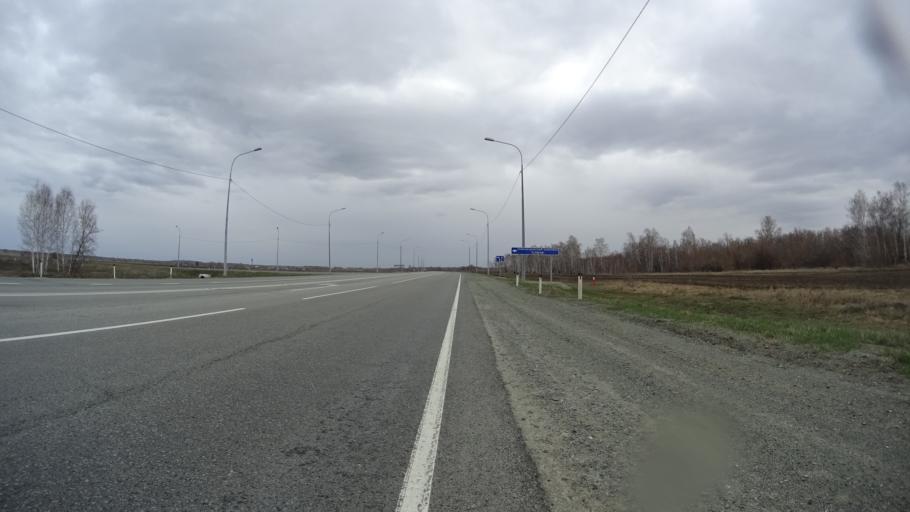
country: RU
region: Chelyabinsk
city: Krasnogorskiy
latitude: 54.6840
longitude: 61.2473
